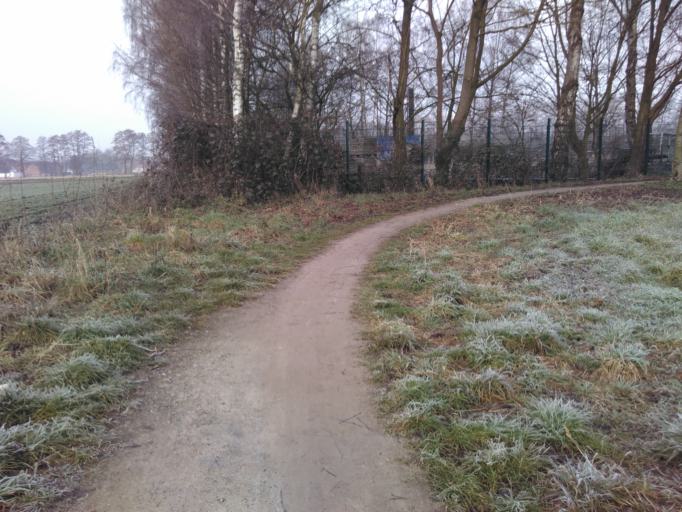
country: DE
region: North Rhine-Westphalia
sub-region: Regierungsbezirk Detmold
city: Verl
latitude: 51.8859
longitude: 8.4920
